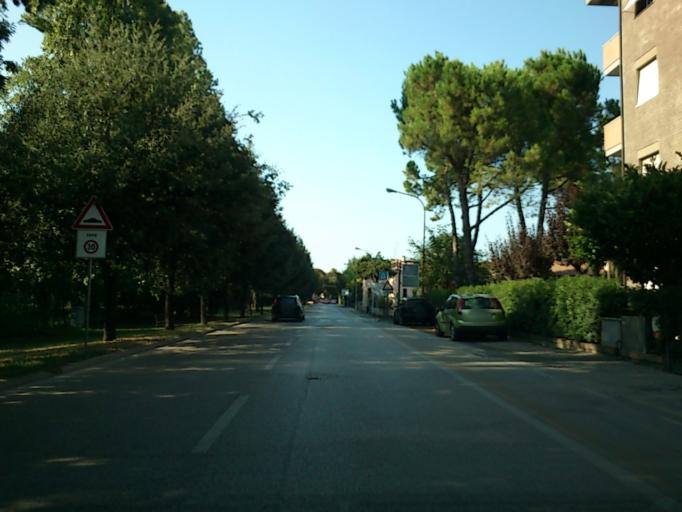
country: IT
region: The Marches
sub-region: Provincia di Pesaro e Urbino
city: Fano
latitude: 43.8352
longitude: 13.0138
